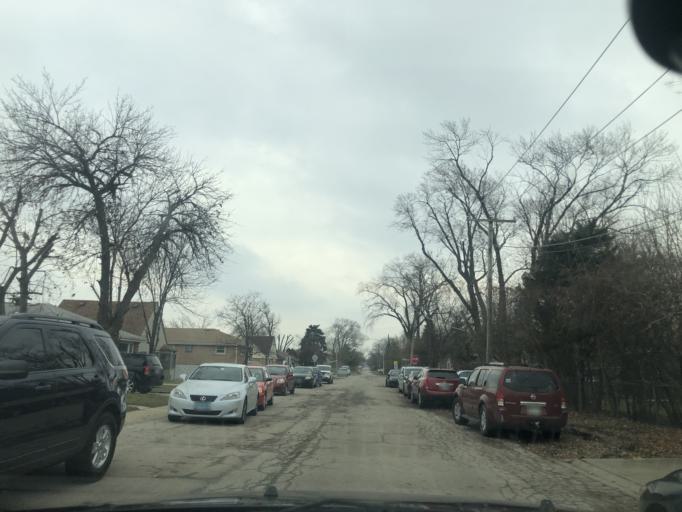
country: US
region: Illinois
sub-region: Cook County
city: Northlake
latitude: 41.9352
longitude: -87.8946
